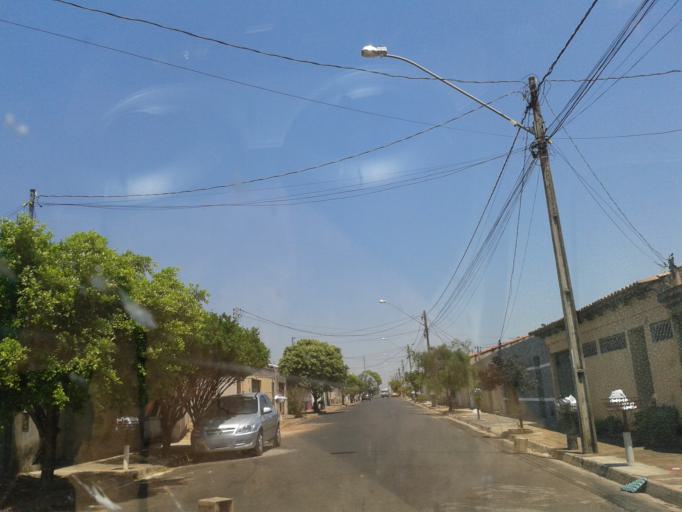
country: BR
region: Minas Gerais
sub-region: Uberlandia
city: Uberlandia
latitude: -18.9606
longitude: -48.3126
